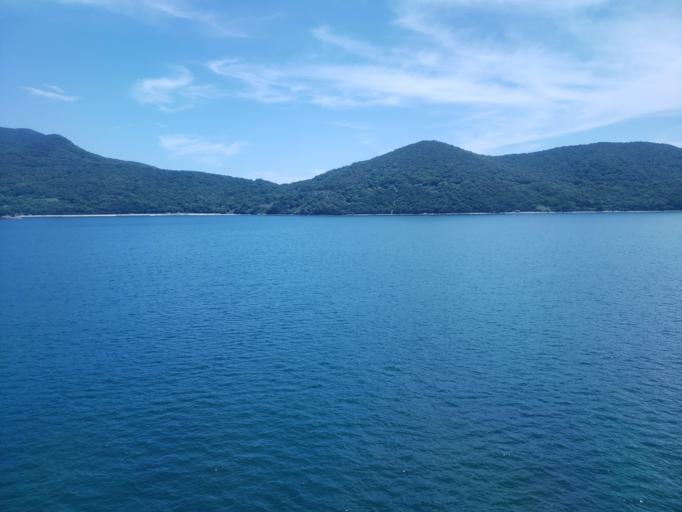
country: JP
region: Kagawa
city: Tonosho
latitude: 34.4383
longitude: 134.3189
